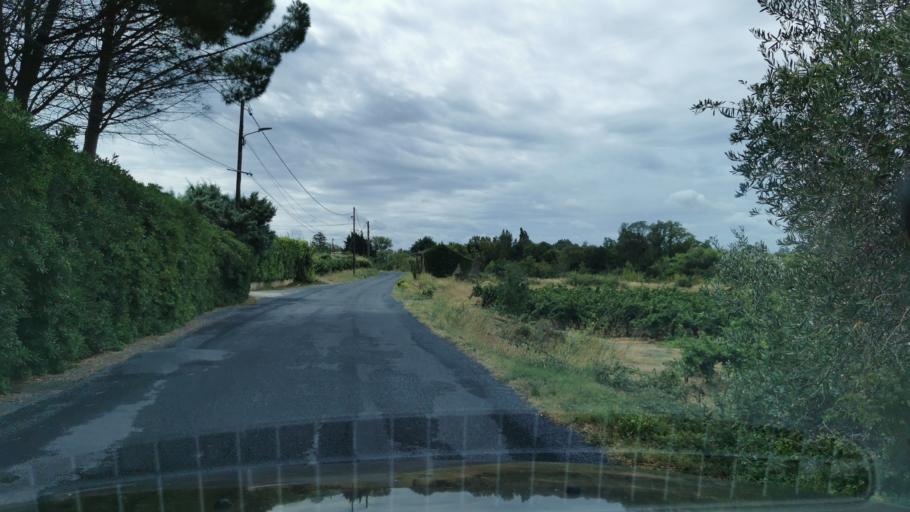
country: FR
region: Languedoc-Roussillon
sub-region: Departement de l'Aude
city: Ornaisons
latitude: 43.1810
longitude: 2.8422
